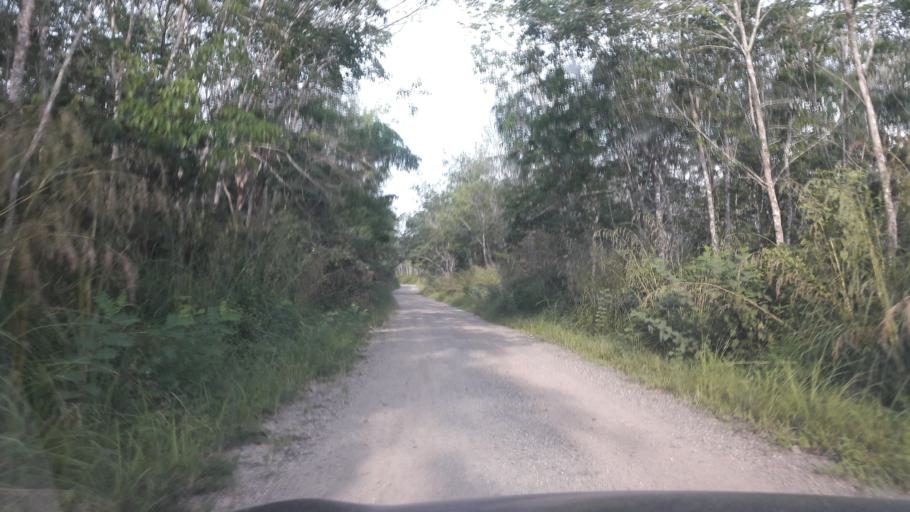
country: ID
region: South Sumatra
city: Gunungmenang
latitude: -3.2680
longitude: 104.0664
